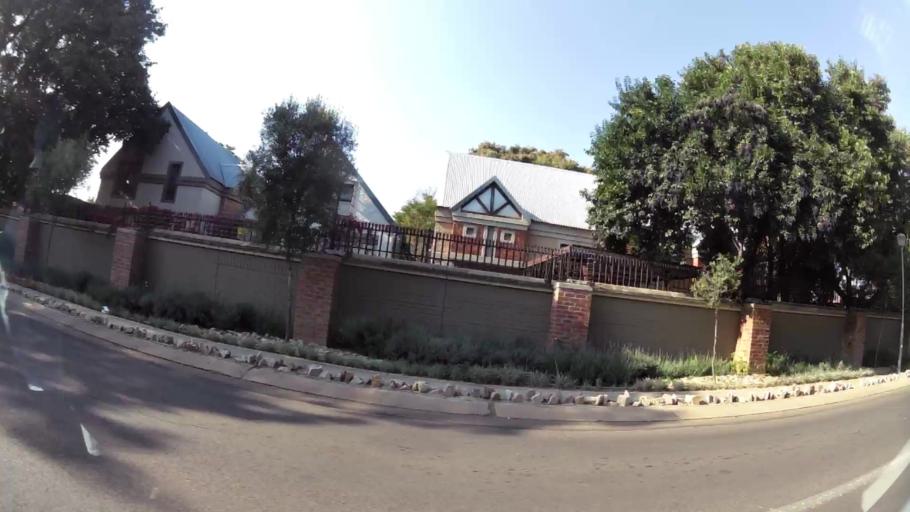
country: ZA
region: Gauteng
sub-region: City of Tshwane Metropolitan Municipality
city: Pretoria
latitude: -25.7667
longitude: 28.3403
